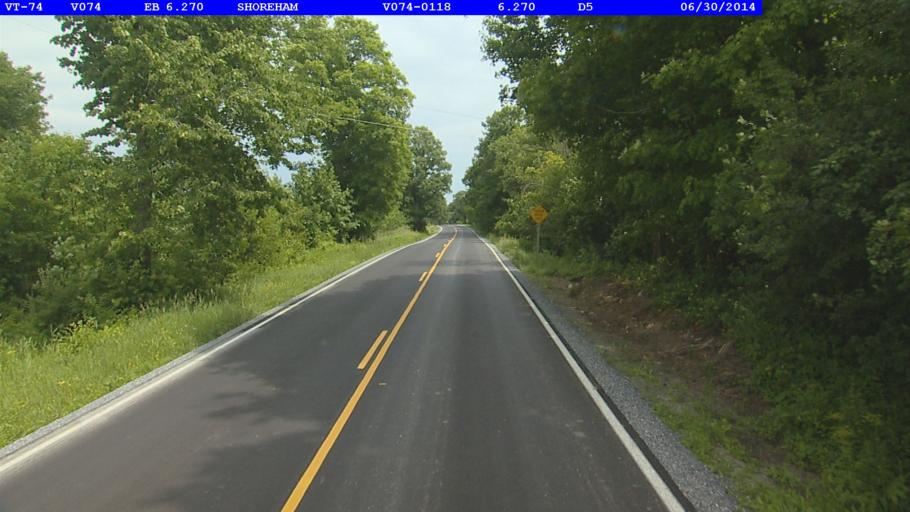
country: US
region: New York
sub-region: Essex County
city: Ticonderoga
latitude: 43.9101
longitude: -73.2966
